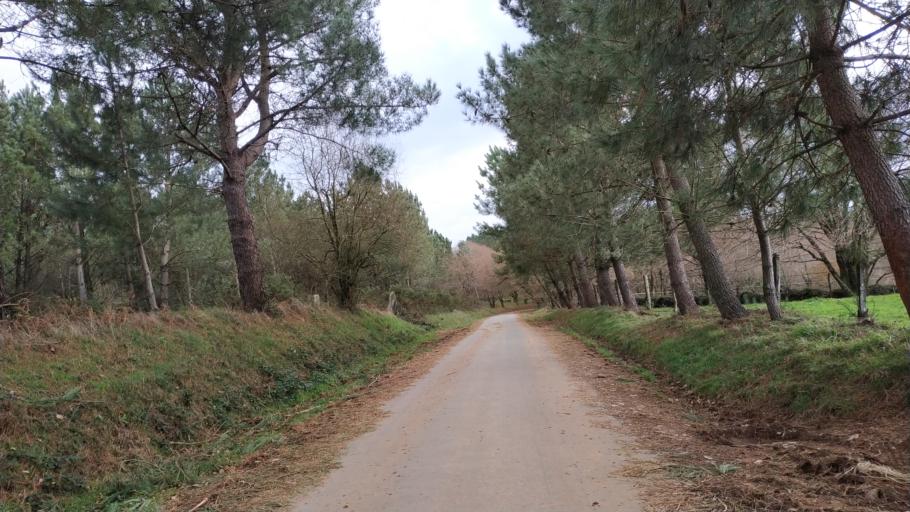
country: ES
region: Galicia
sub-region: Provincia de Pontevedra
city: Silleda
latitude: 42.7715
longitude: -8.1651
